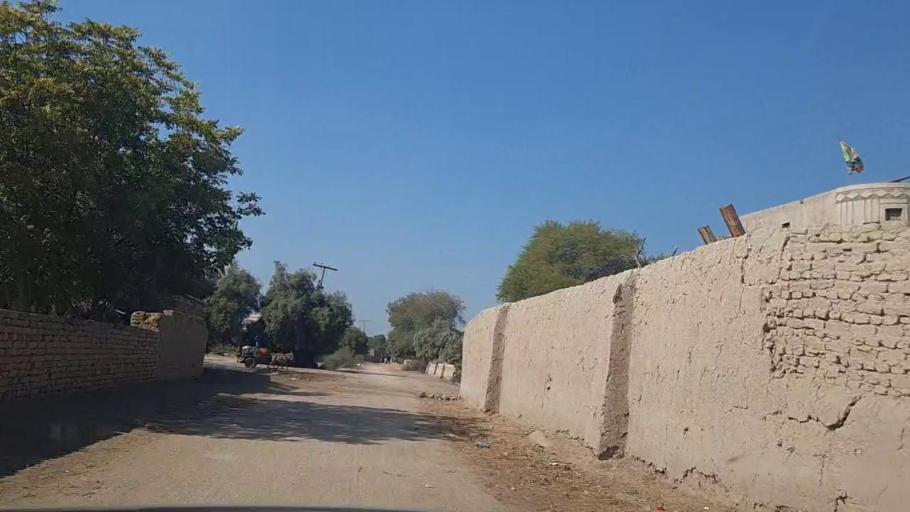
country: PK
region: Sindh
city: Sehwan
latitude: 26.2727
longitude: 68.0348
